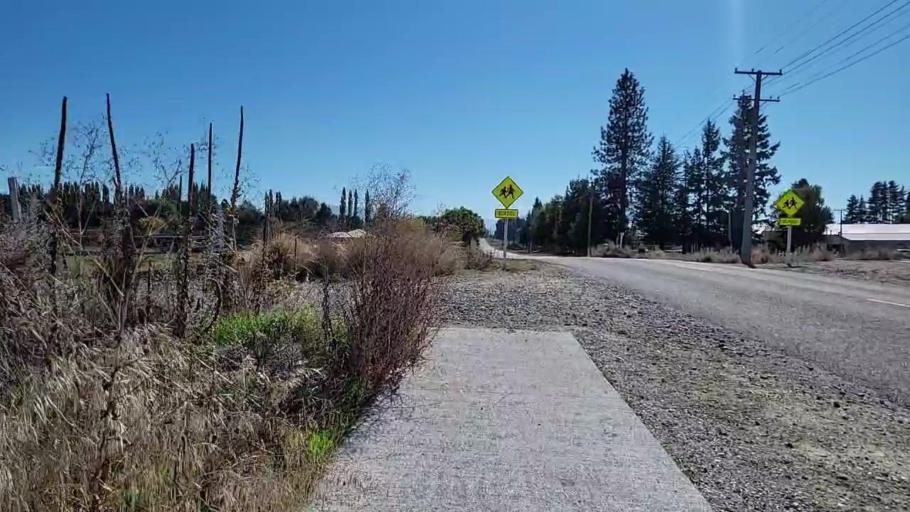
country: NZ
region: Otago
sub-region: Queenstown-Lakes District
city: Wanaka
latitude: -45.0926
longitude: 169.6018
